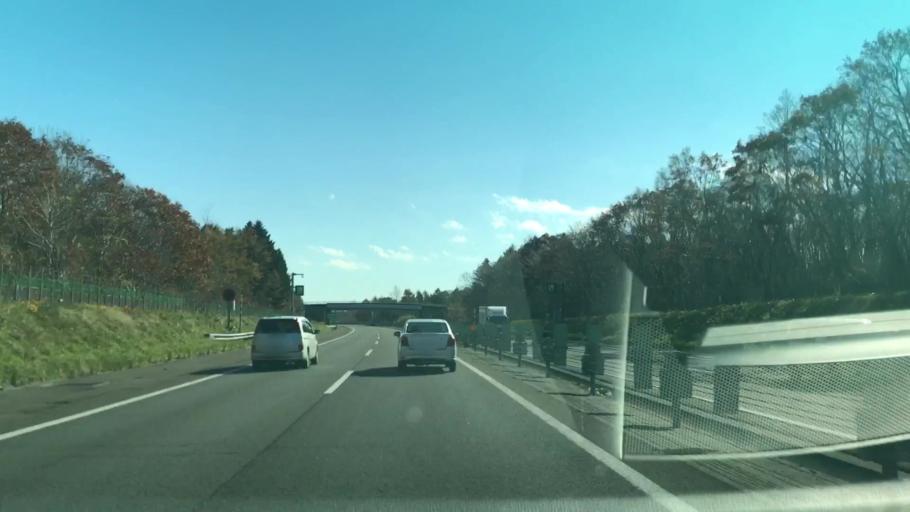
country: JP
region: Hokkaido
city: Chitose
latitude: 42.8593
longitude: 141.5605
